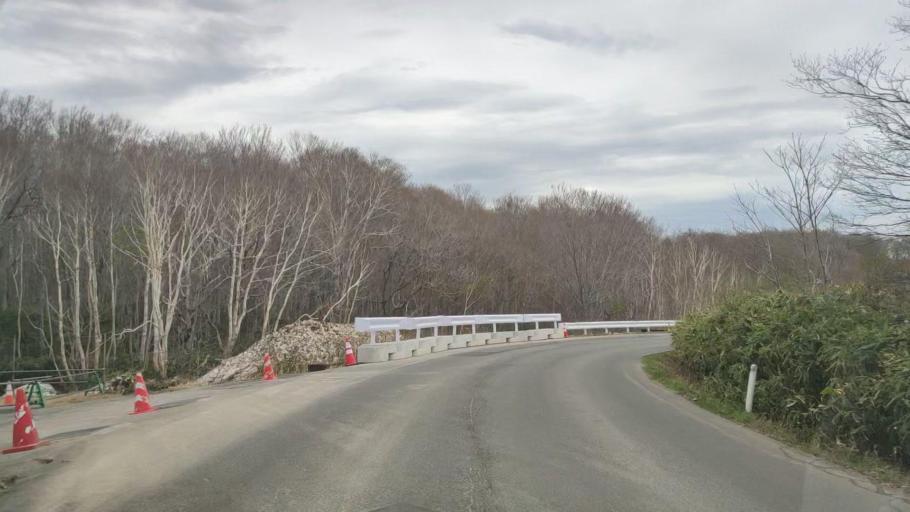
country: JP
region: Aomori
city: Aomori Shi
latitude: 40.6889
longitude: 140.9220
